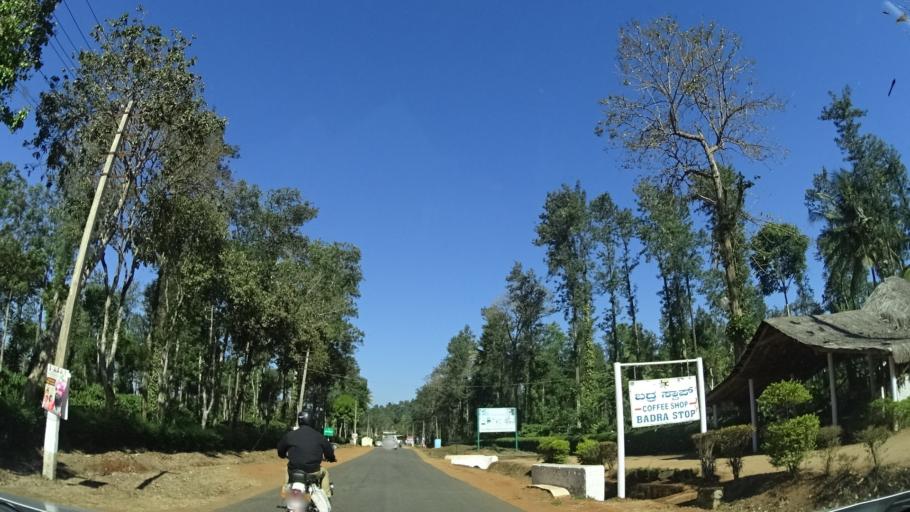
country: IN
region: Karnataka
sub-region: Chikmagalur
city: Koppa
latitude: 13.3521
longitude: 75.4737
